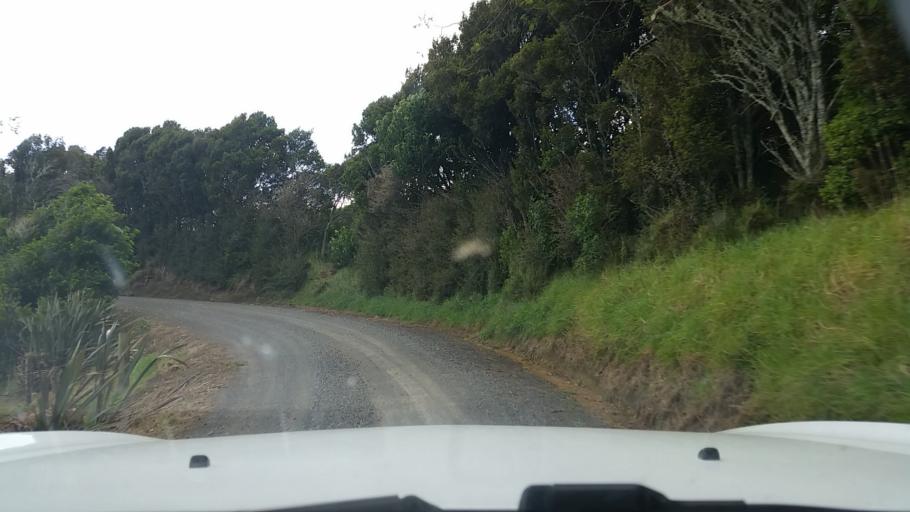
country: NZ
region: Waikato
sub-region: Hauraki District
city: Ngatea
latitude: -37.4601
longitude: 175.4696
